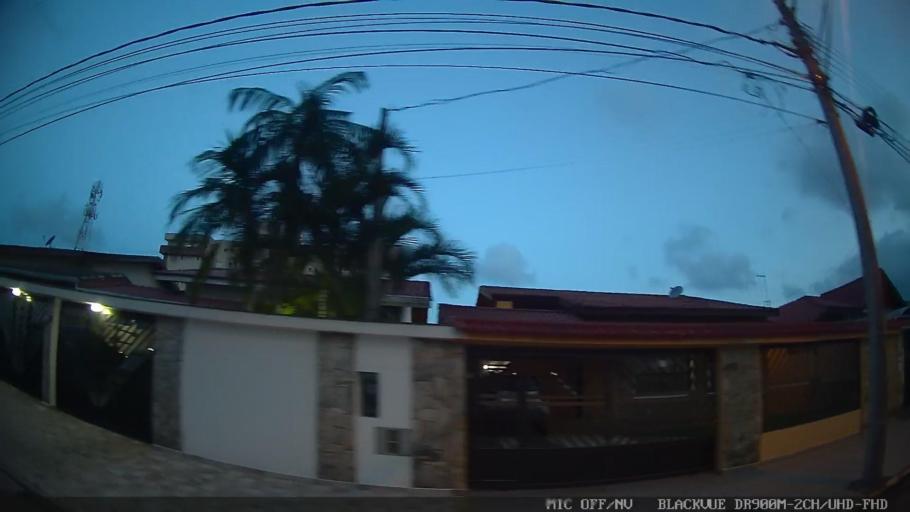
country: BR
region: Sao Paulo
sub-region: Peruibe
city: Peruibe
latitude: -24.3179
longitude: -46.9960
